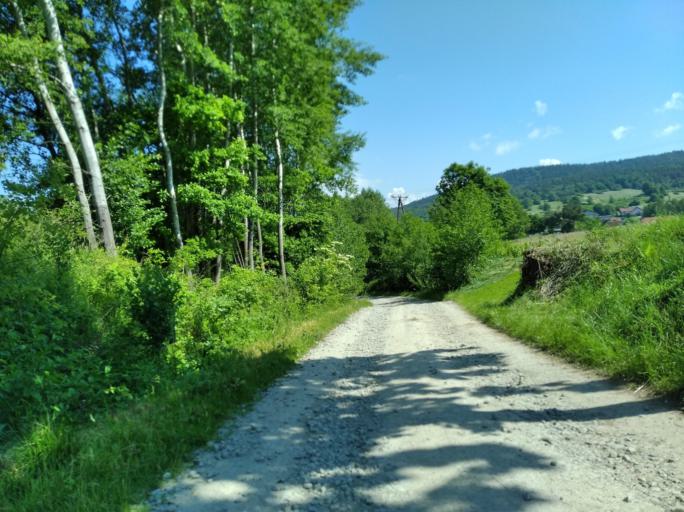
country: PL
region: Subcarpathian Voivodeship
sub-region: Powiat krosnienski
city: Odrzykon
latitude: 49.7770
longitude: 21.7608
